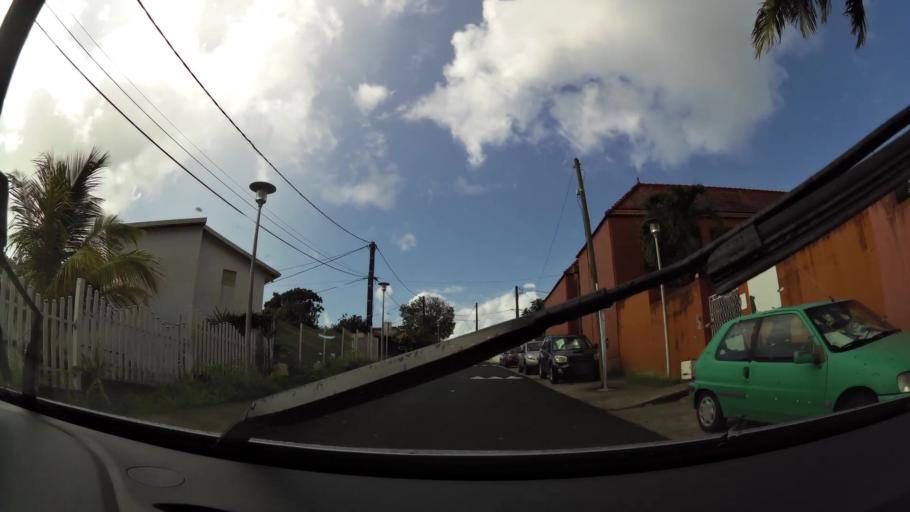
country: MQ
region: Martinique
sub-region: Martinique
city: Les Trois-Ilets
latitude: 14.5376
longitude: -61.0353
